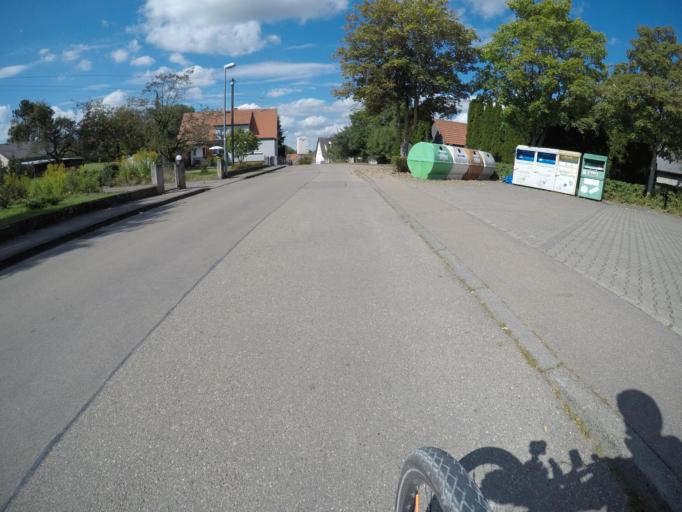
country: DE
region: Bavaria
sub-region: Swabia
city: Wittislingen
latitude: 48.6154
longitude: 10.4184
